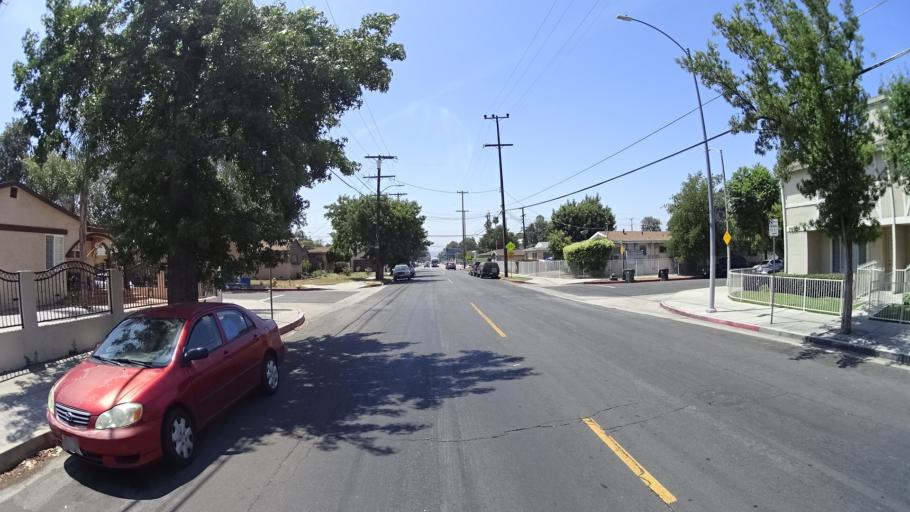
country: US
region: California
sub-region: Los Angeles County
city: Van Nuys
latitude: 34.2096
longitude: -118.4575
